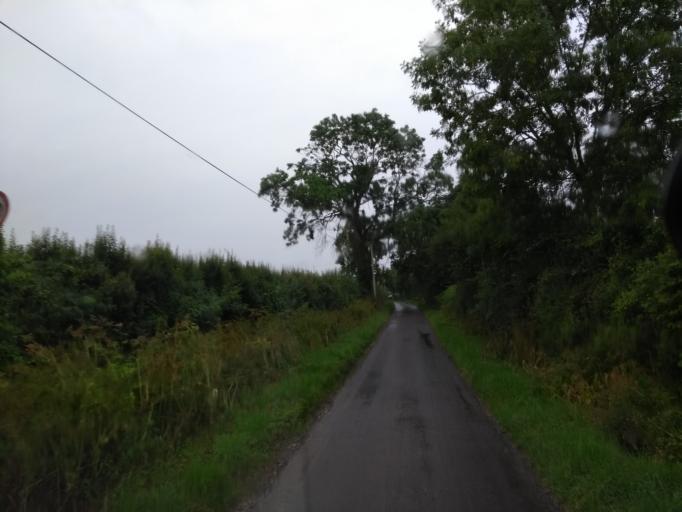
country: GB
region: England
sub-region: Somerset
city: Street
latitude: 51.0939
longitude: -2.6822
